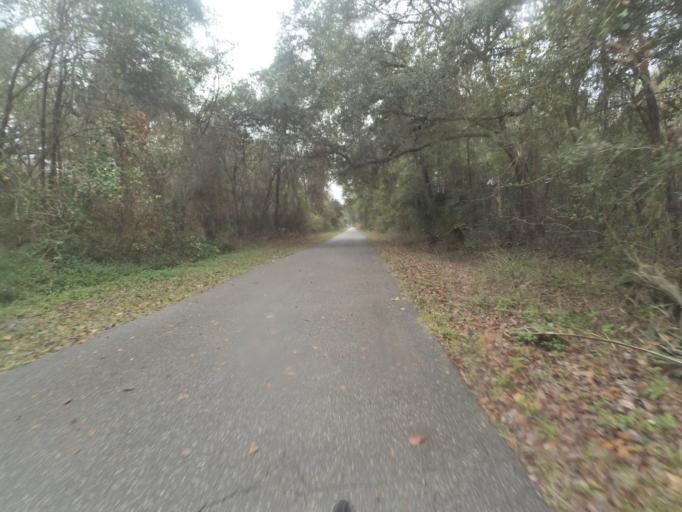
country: US
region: Florida
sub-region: Alachua County
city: Hawthorne
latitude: 29.5987
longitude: -82.1569
